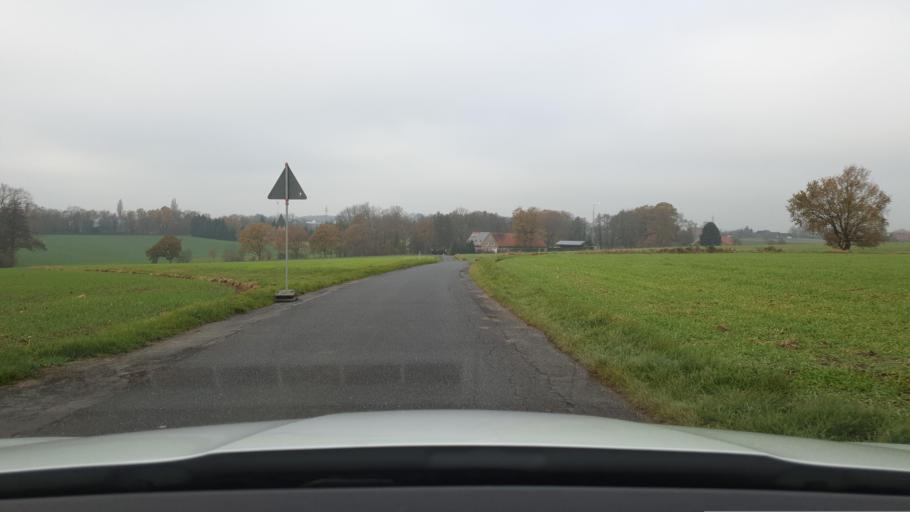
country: DE
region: North Rhine-Westphalia
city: Bad Oeynhausen
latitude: 52.2253
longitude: 8.7565
